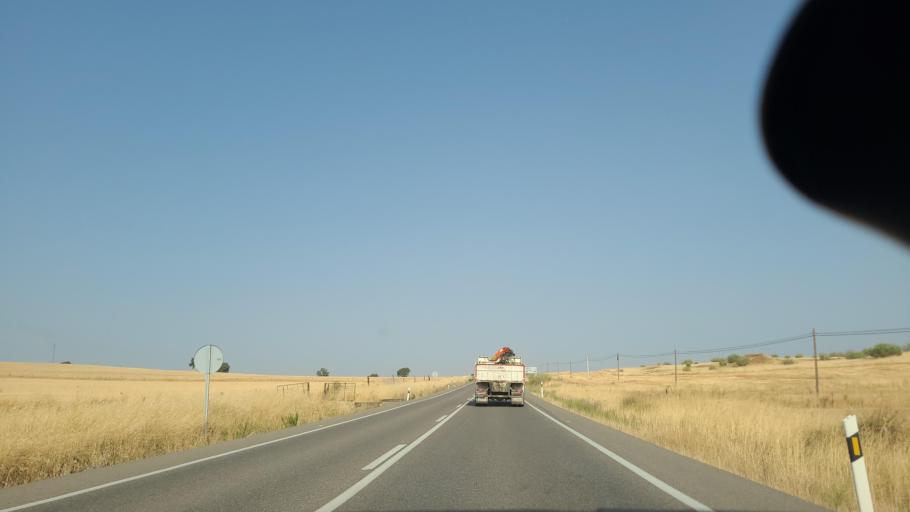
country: ES
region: Andalusia
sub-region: Province of Cordoba
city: Penarroya-Pueblonuevo
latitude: 38.2948
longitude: -5.2858
